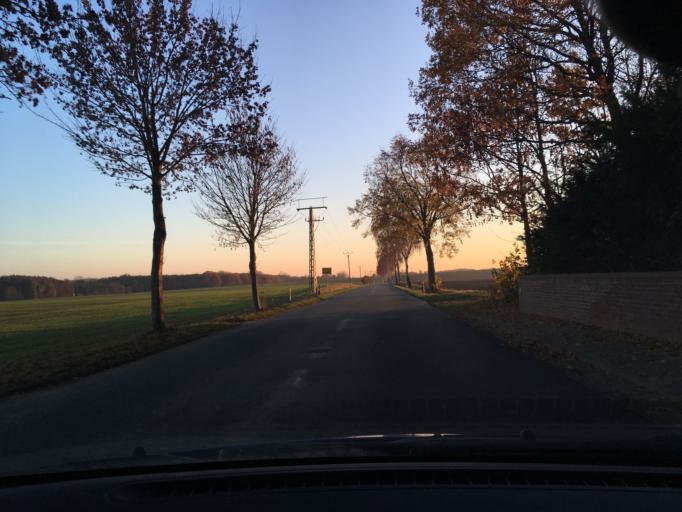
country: DE
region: Lower Saxony
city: Natendorf
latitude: 53.0957
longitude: 10.4674
